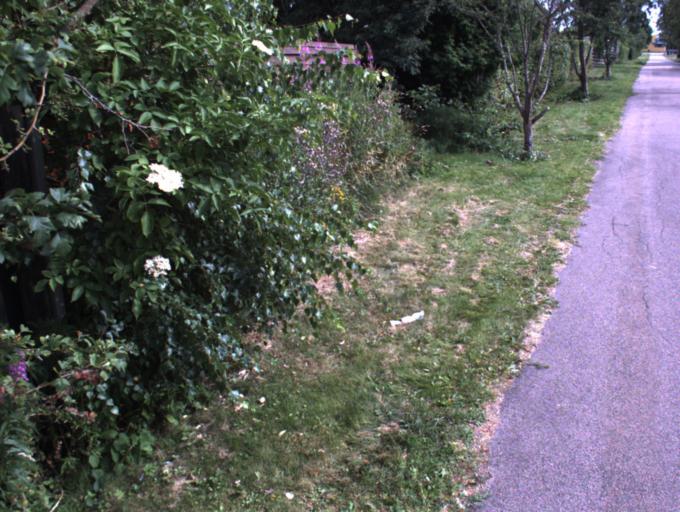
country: SE
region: Skane
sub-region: Helsingborg
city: Gantofta
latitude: 55.9896
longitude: 12.8024
